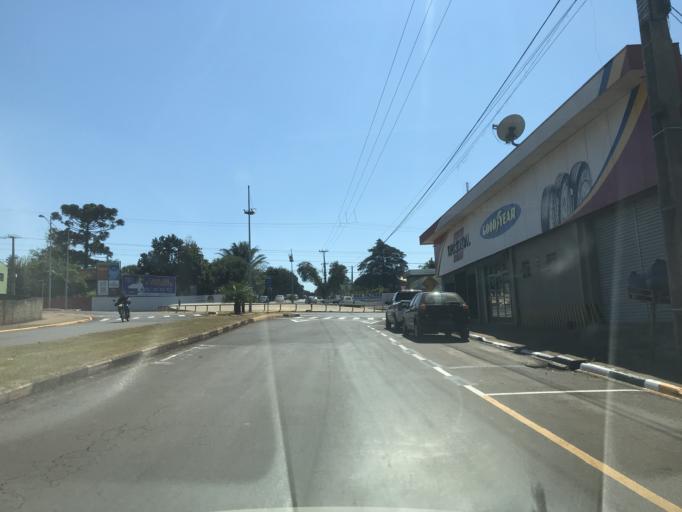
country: BR
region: Parana
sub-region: Toledo
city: Toledo
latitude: -24.7274
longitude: -53.7360
